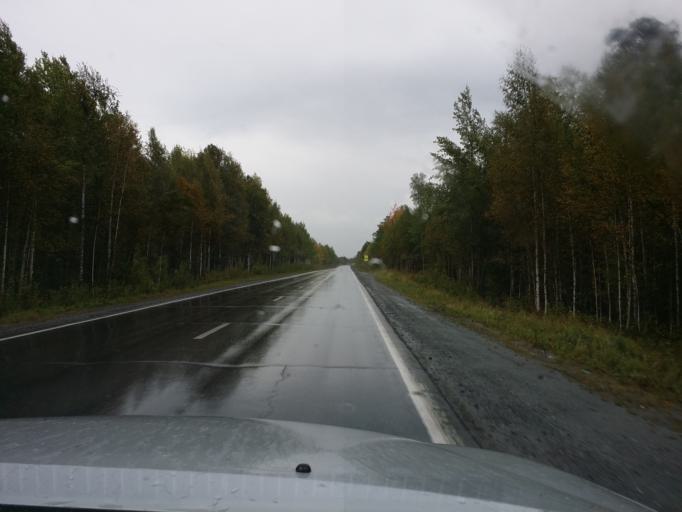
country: RU
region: Khanty-Mansiyskiy Avtonomnyy Okrug
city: Megion
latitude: 61.1617
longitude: 75.6695
